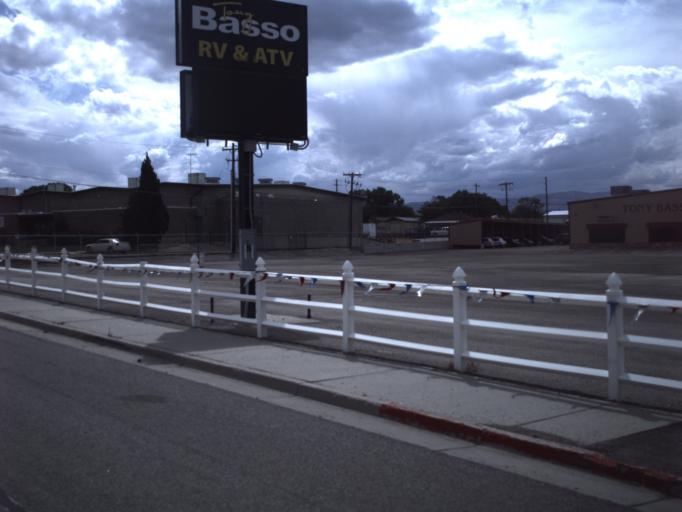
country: US
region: Utah
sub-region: Carbon County
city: Price
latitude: 39.5843
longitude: -110.8140
